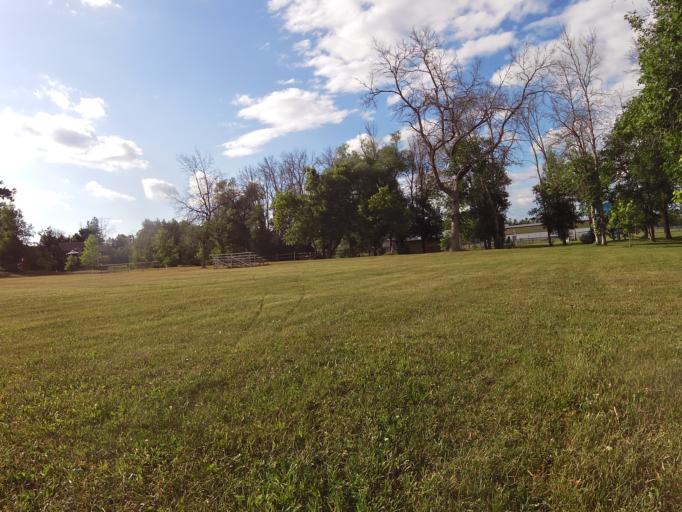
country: CA
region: Ontario
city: Arnprior
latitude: 45.3290
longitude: -76.2892
